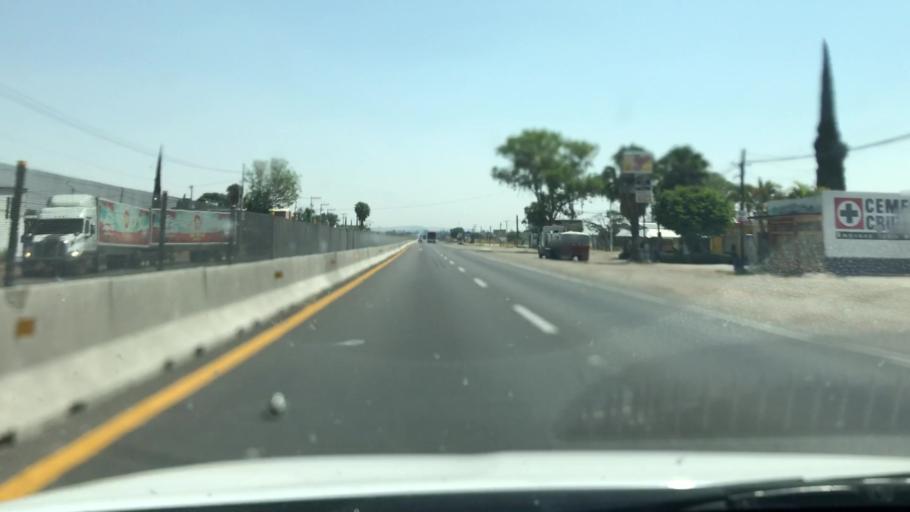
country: MX
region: Guanajuato
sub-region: Abasolo
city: San Bernardo Pena Blanca
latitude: 20.4687
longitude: -101.5059
